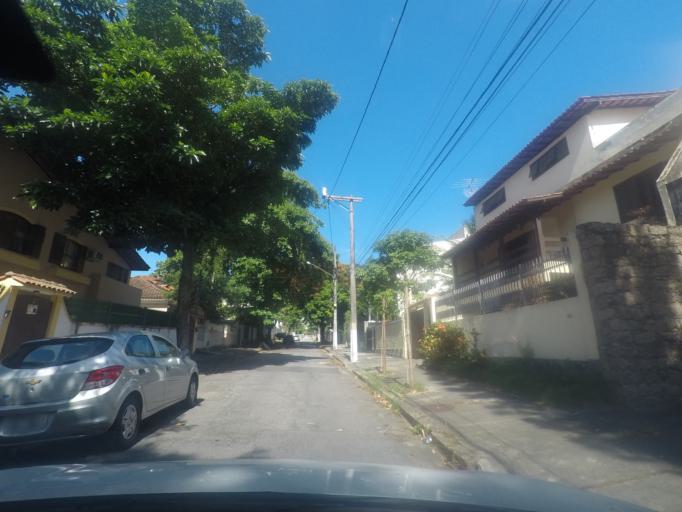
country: BR
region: Rio de Janeiro
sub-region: Niteroi
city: Niteroi
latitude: -22.9210
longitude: -43.0893
